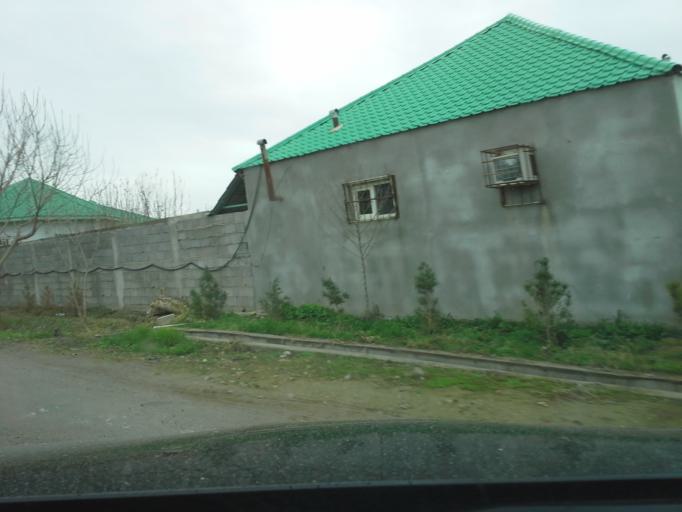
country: TM
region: Ahal
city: Abadan
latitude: 37.9651
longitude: 58.2294
